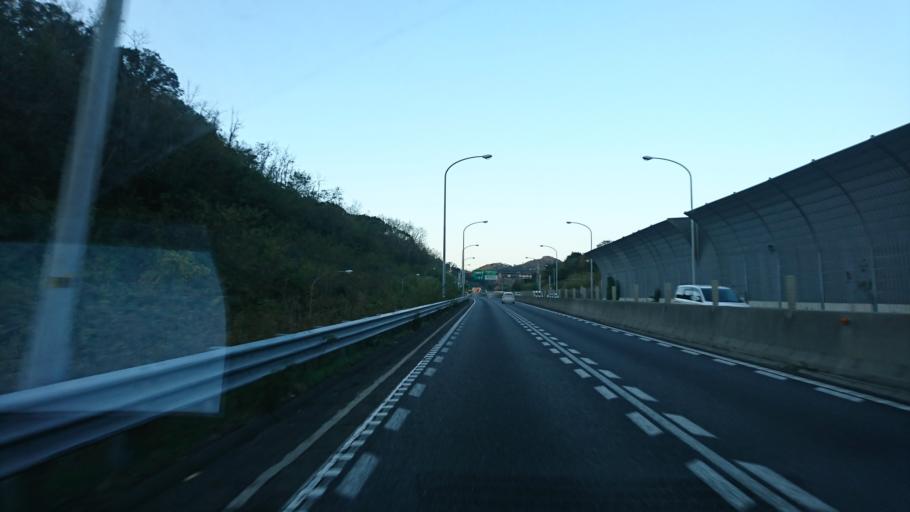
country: JP
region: Hyogo
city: Kobe
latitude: 34.6545
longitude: 135.1118
